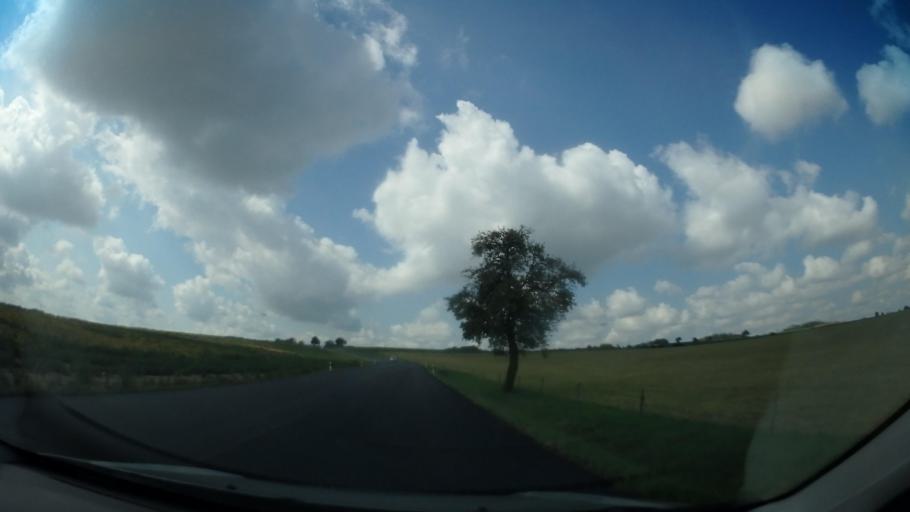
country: CZ
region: Central Bohemia
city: Cervene Pecky
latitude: 49.9486
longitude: 15.2275
